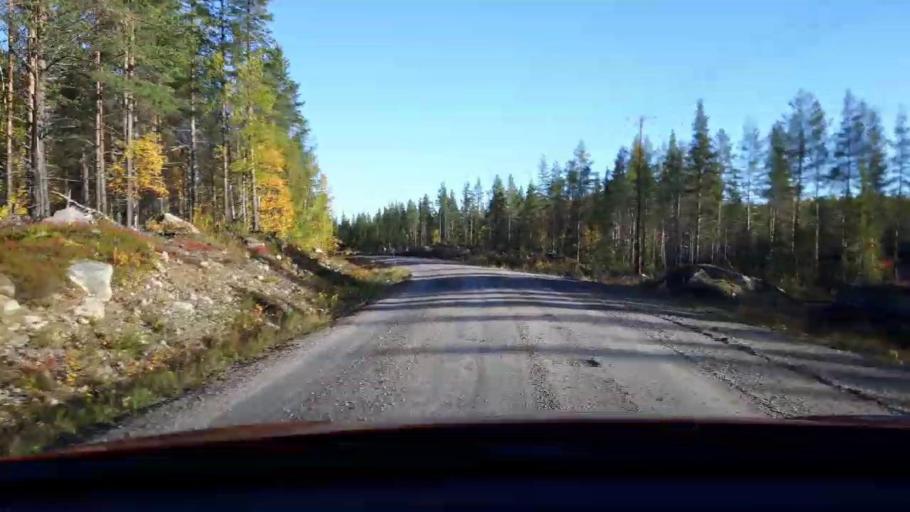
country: SE
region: Jaemtland
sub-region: Stroemsunds Kommun
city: Stroemsund
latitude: 64.3859
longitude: 15.1517
